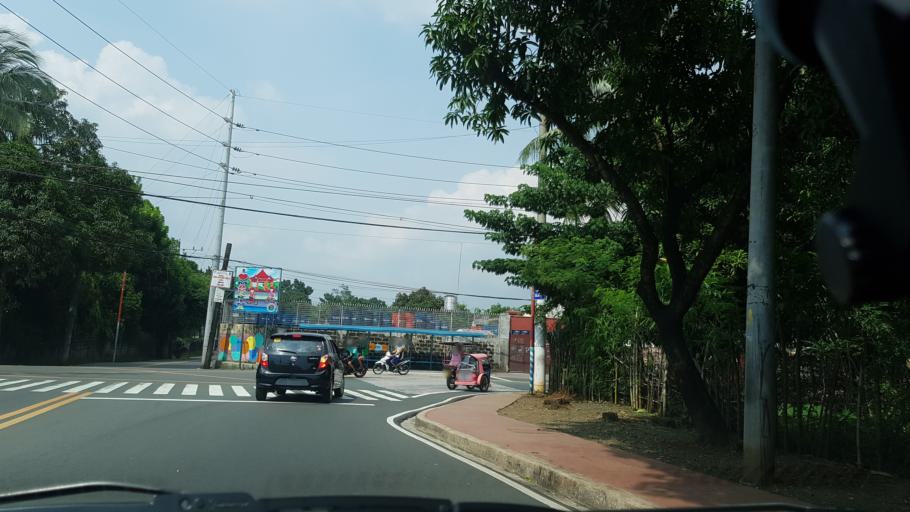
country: PH
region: Calabarzon
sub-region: Province of Rizal
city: San Mateo
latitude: 14.6627
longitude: 121.1187
